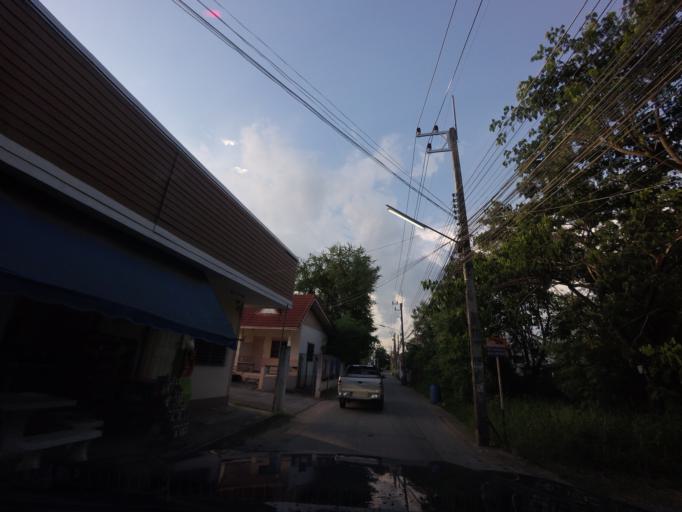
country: TH
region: Khon Kaen
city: Khon Kaen
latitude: 16.4243
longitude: 102.8619
